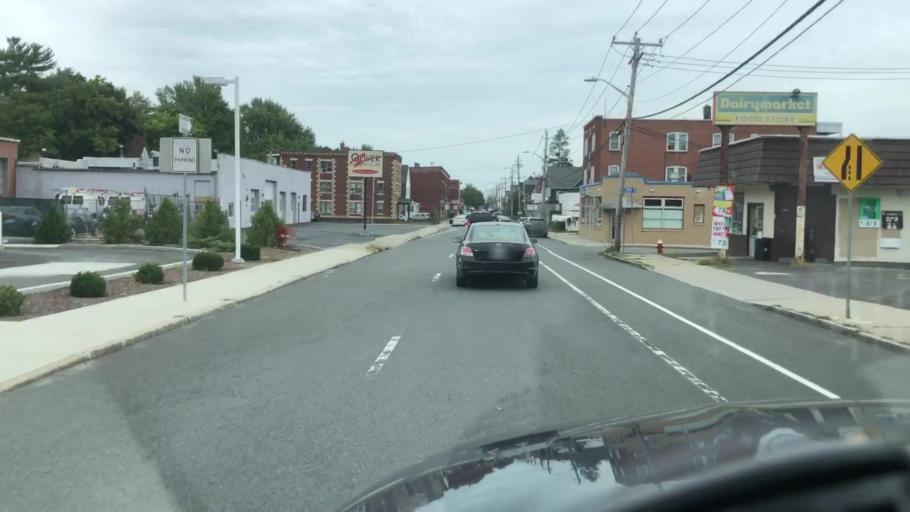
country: US
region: Massachusetts
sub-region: Hampden County
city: Holyoke
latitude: 42.2109
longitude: -72.6284
